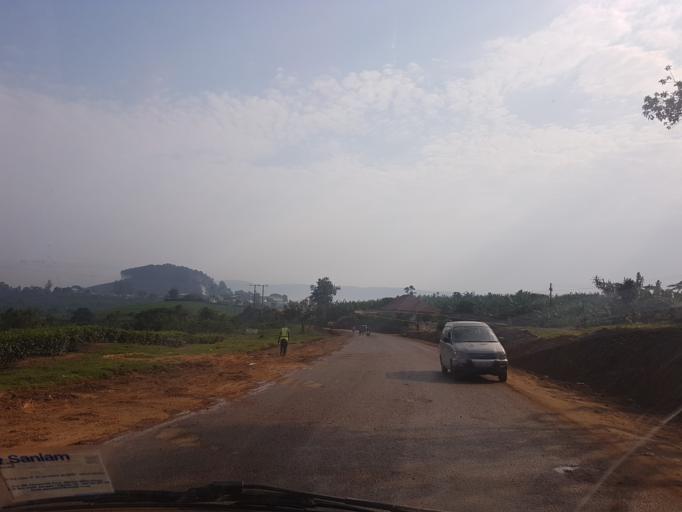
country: UG
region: Western Region
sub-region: Rubirizi District
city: Rubirizi
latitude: -0.4279
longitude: 30.1120
